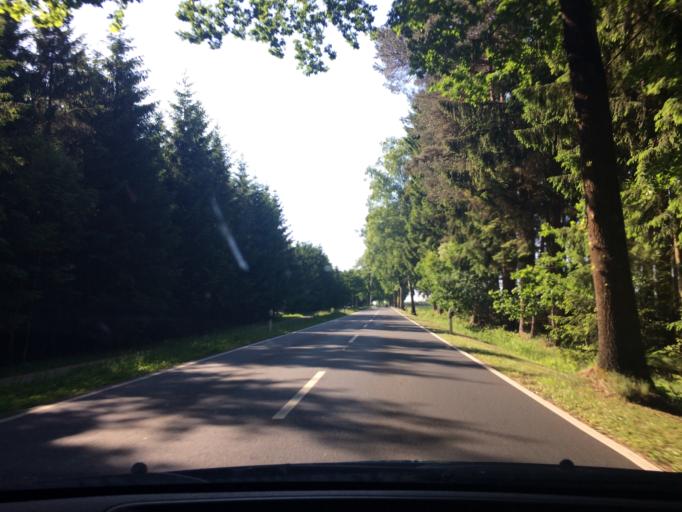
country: DE
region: Lower Saxony
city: Bad Fallingbostel
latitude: 52.9149
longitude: 9.7133
